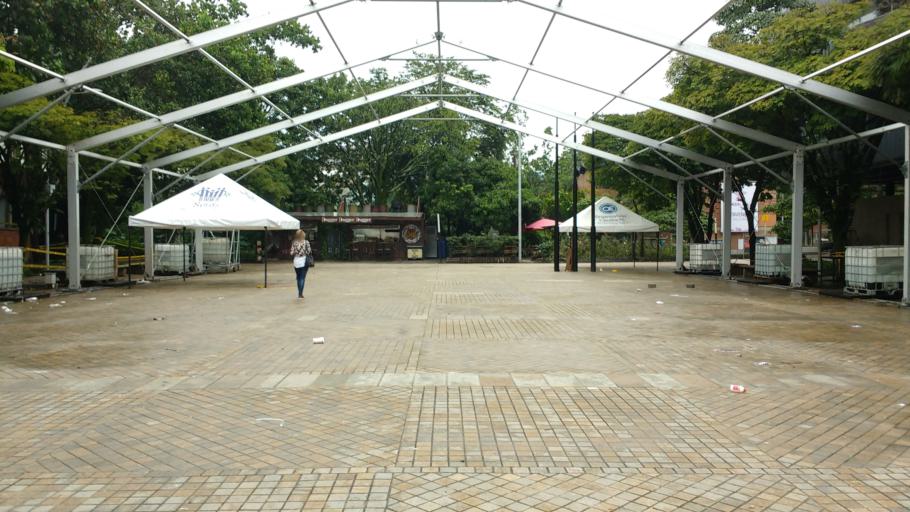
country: CO
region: Antioquia
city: Itagui
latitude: 6.2006
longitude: -75.5784
